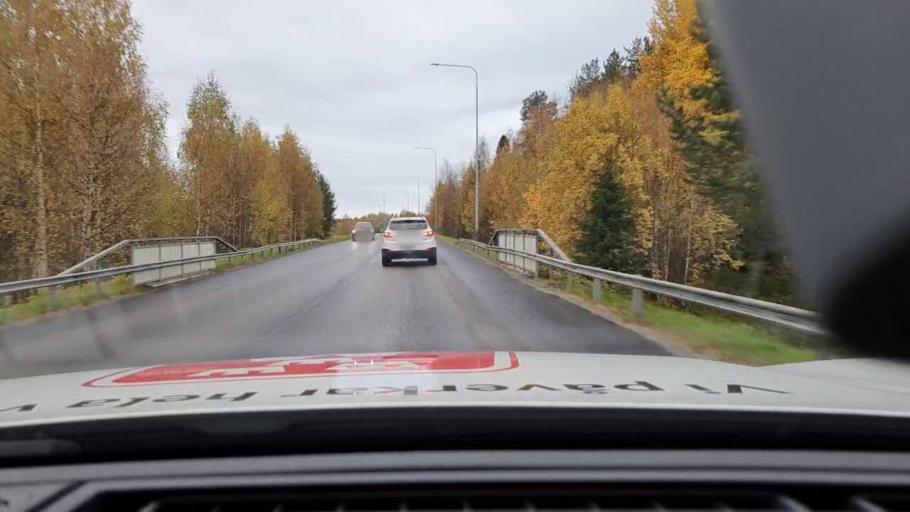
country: SE
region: Norrbotten
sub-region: Bodens Kommun
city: Saevast
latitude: 65.7648
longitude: 21.7388
